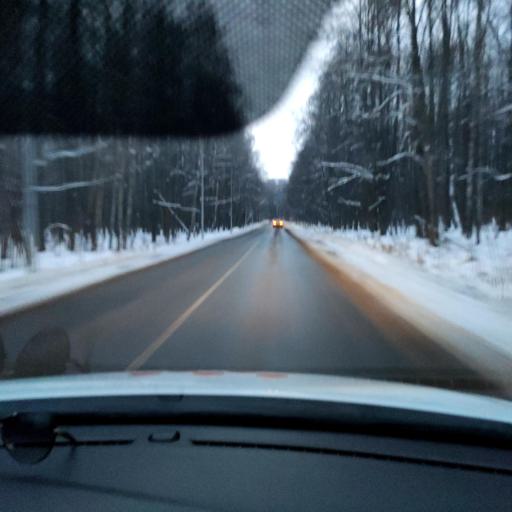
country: RU
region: Tatarstan
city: Vysokaya Gora
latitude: 55.9304
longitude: 49.1926
